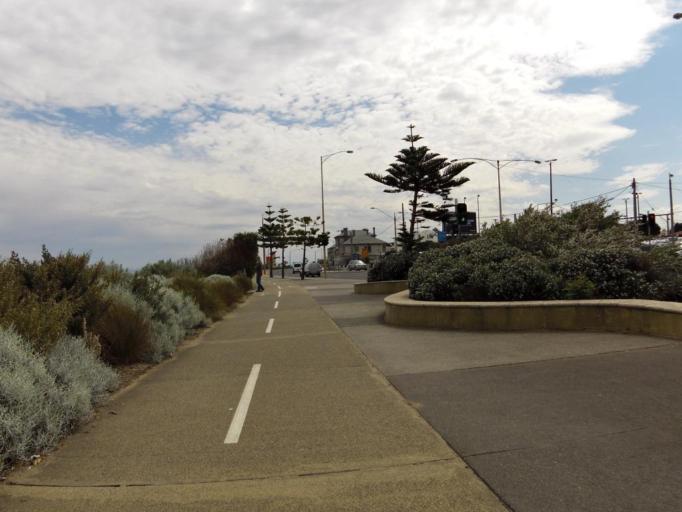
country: AU
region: Victoria
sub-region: Bayside
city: Hampton
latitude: -37.9279
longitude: 144.9888
